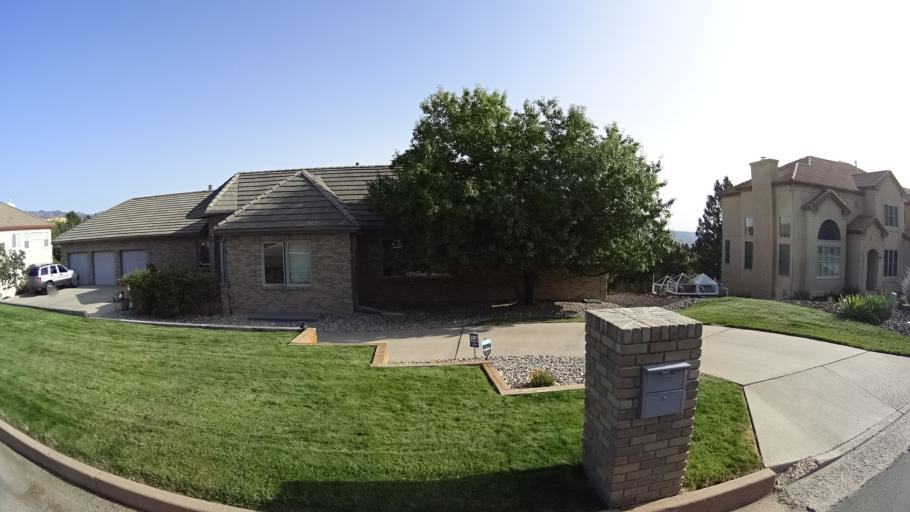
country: US
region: Colorado
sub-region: El Paso County
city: Manitou Springs
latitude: 38.8225
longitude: -104.8782
